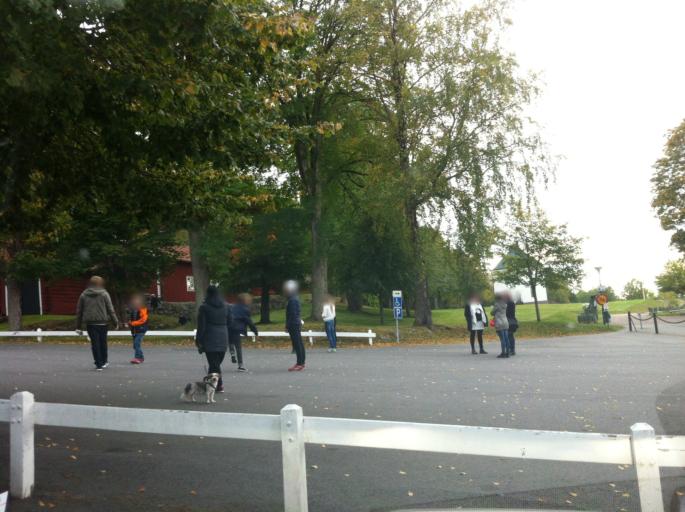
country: SE
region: OEstergoetland
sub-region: Motala Kommun
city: Motala
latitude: 58.6127
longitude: 14.9476
